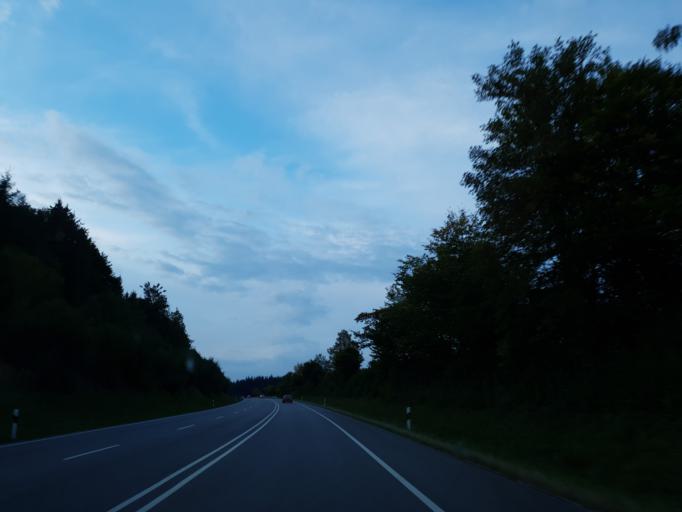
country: DE
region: Bavaria
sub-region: Swabia
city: Biessenhofen
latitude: 47.8407
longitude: 10.6754
